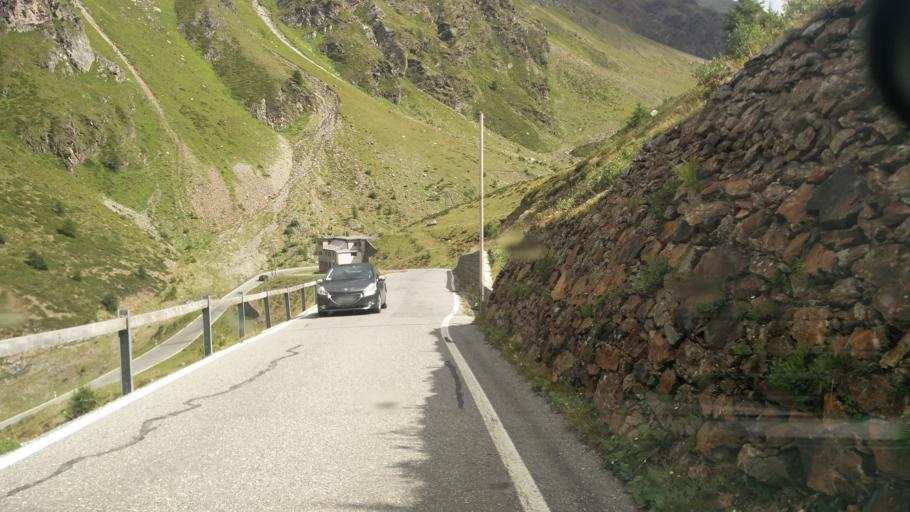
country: IT
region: Trentino-Alto Adige
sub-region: Bolzano
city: Tubre
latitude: 46.5579
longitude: 10.4338
